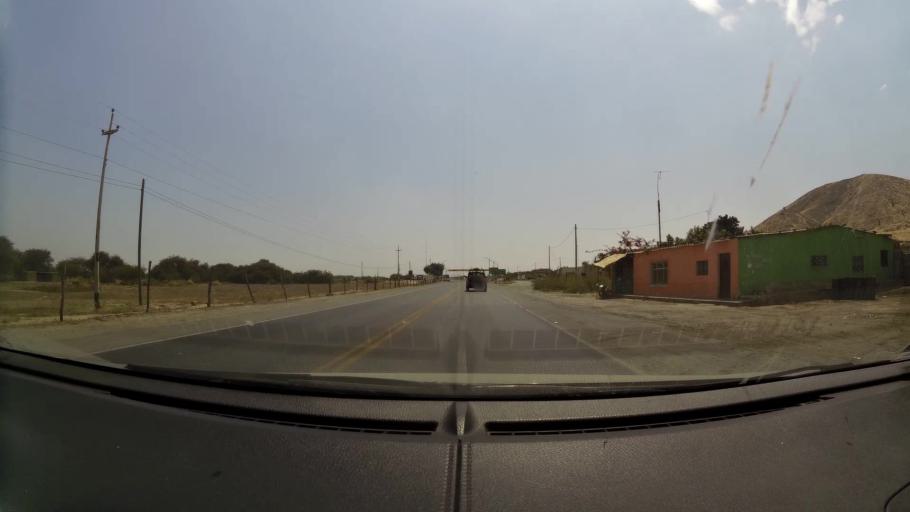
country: PE
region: La Libertad
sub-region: Chepen
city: Pacanga
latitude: -7.1134
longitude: -79.4948
